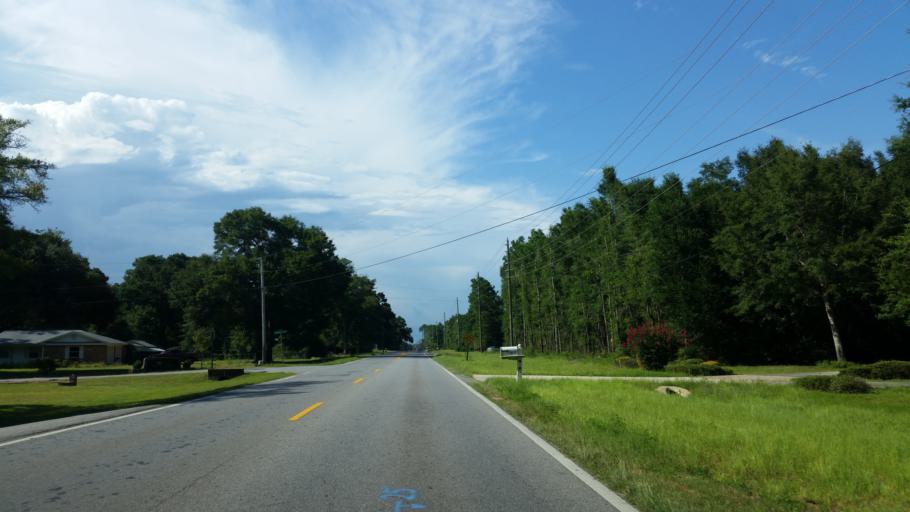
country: US
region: Florida
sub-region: Santa Rosa County
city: Pace
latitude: 30.6130
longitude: -87.1317
